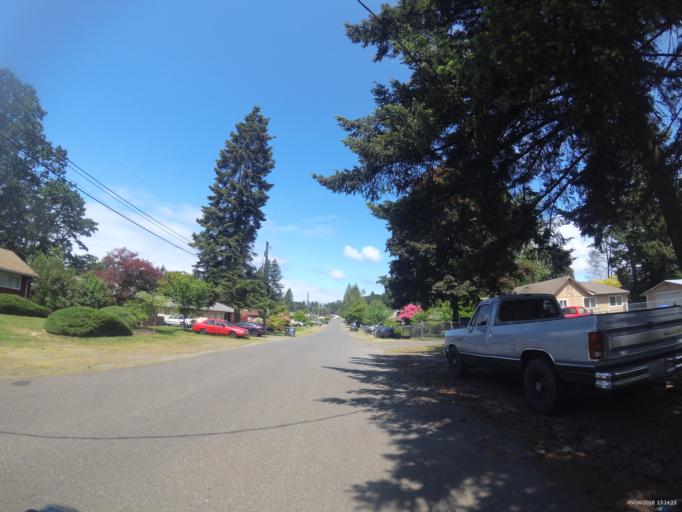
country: US
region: Washington
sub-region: Pierce County
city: Lakewood
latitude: 47.1800
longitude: -122.5225
